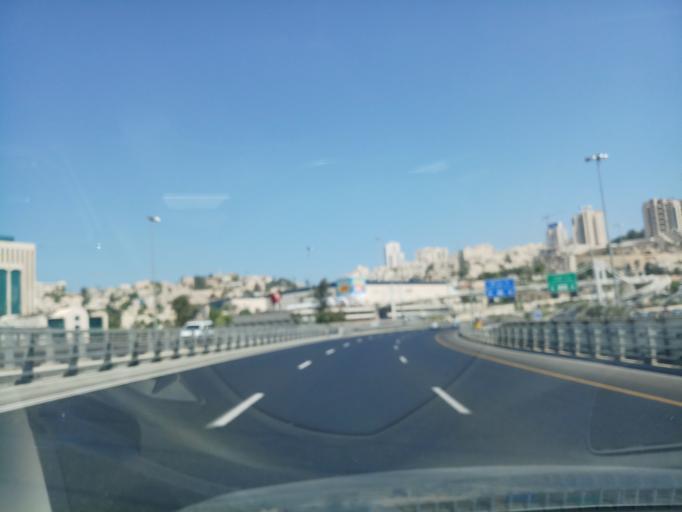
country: PS
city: Khallat Hamamah
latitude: 31.7489
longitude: 35.1897
